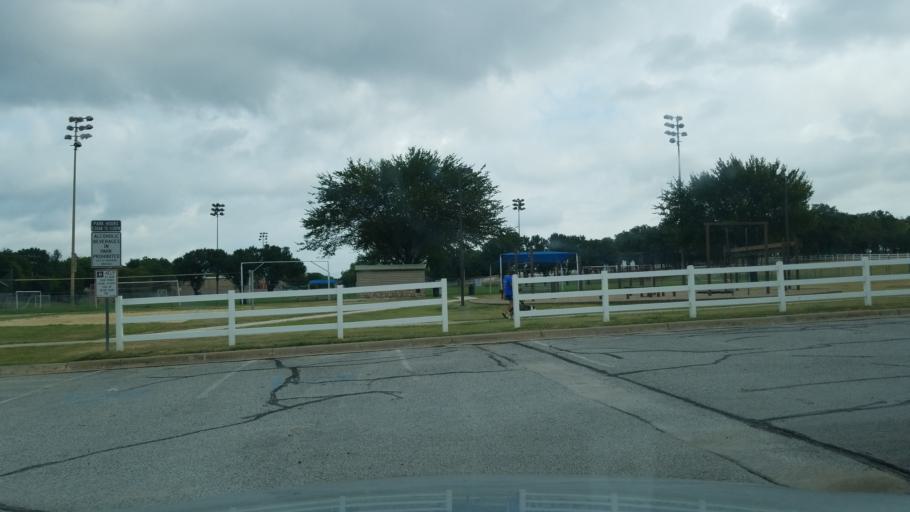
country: US
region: Texas
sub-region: Tarrant County
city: Euless
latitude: 32.8479
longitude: -97.1024
